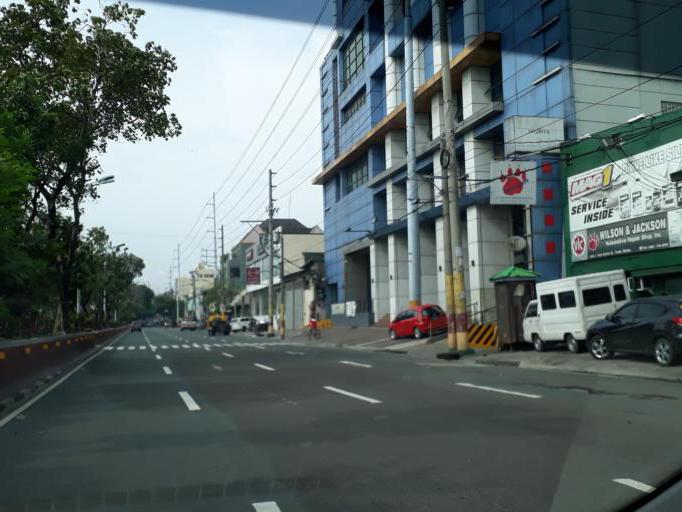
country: PH
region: Metro Manila
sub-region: City of Manila
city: Manila
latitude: 14.6285
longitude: 120.9794
